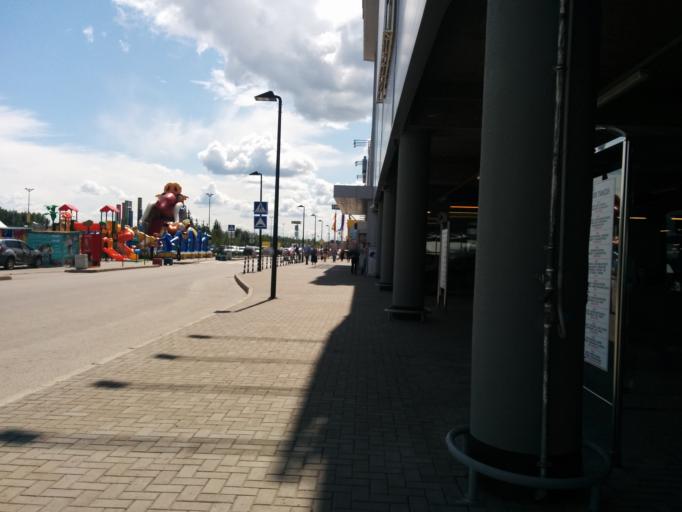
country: RU
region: Bashkortostan
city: Ufa
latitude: 54.6765
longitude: 55.9308
